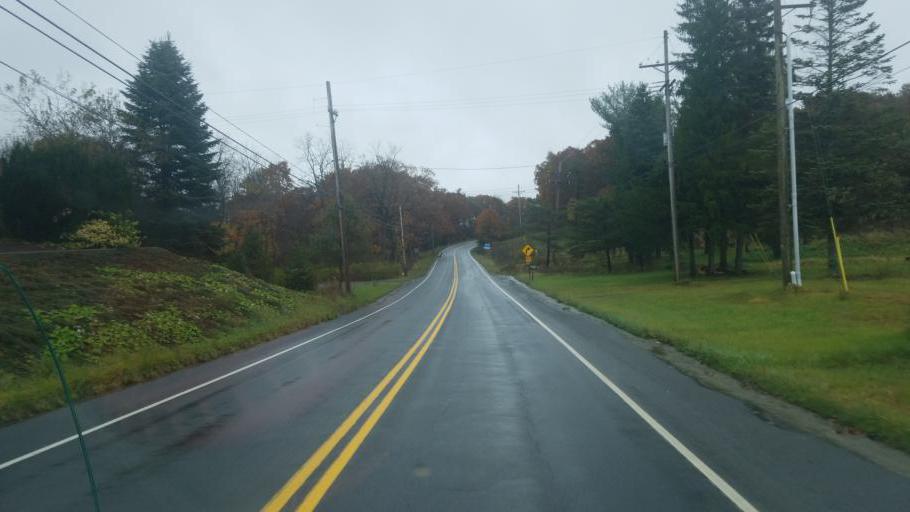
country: US
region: Pennsylvania
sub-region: Centre County
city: Milesburg
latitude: 41.0299
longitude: -77.9634
